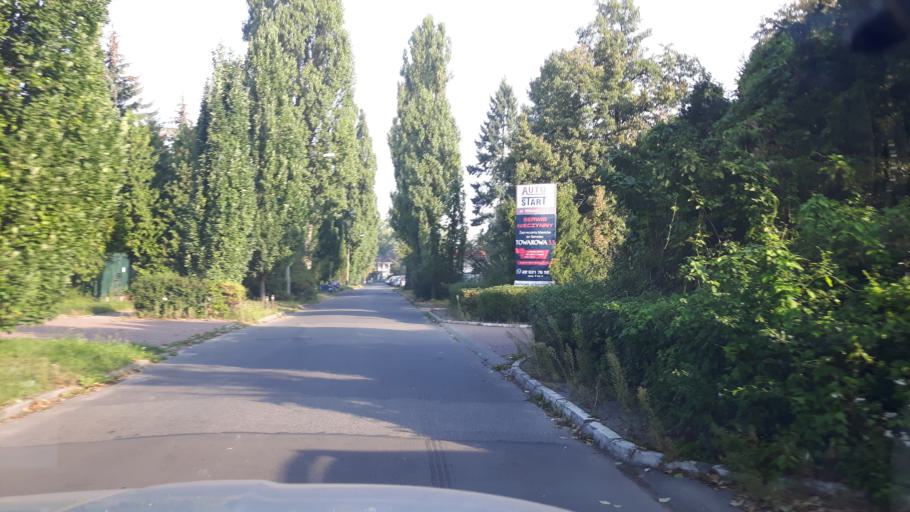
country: PL
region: Masovian Voivodeship
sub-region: Warszawa
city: Zoliborz
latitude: 52.2785
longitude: 21.0147
